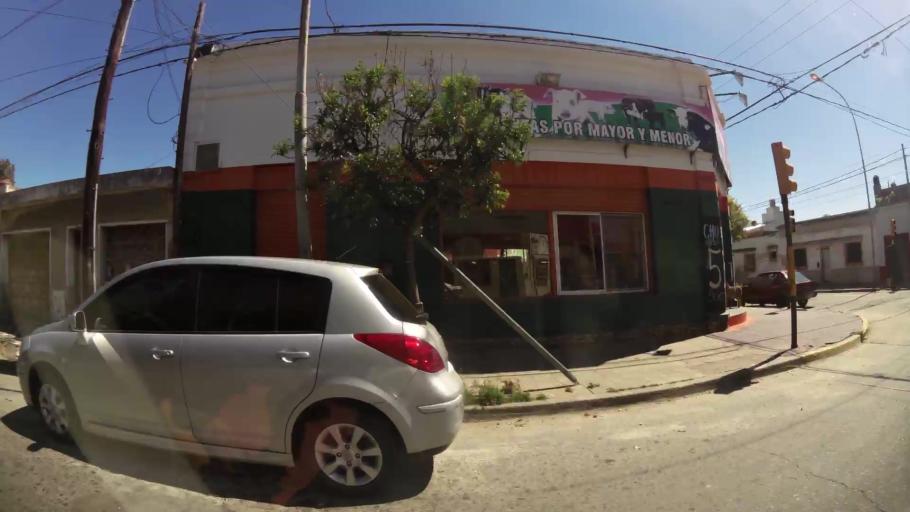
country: AR
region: Cordoba
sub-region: Departamento de Capital
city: Cordoba
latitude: -31.4235
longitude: -64.1584
